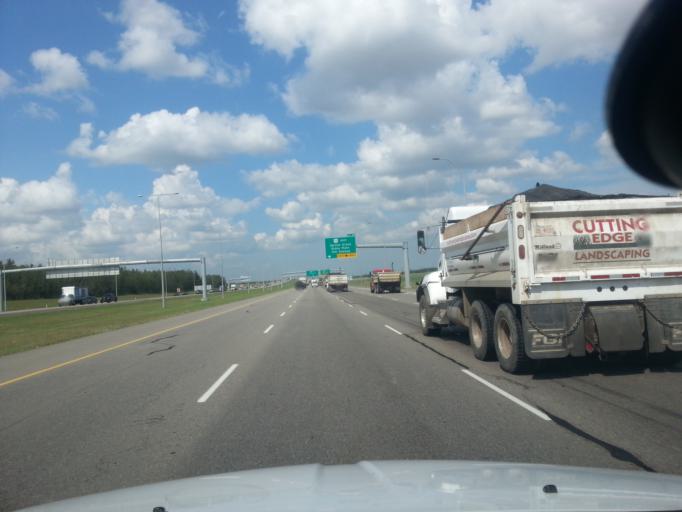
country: CA
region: Alberta
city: St. Albert
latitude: 53.5275
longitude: -113.6589
